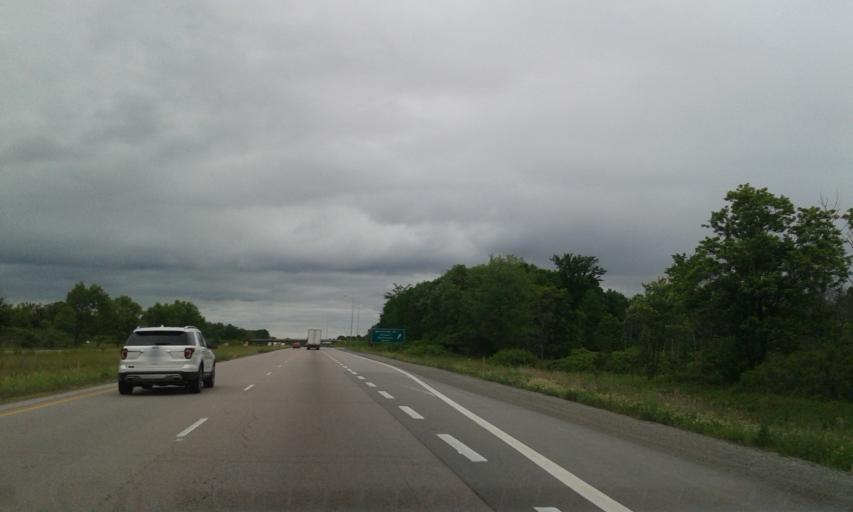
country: US
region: New York
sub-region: Jefferson County
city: Alexandria Bay
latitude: 44.4680
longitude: -75.8743
